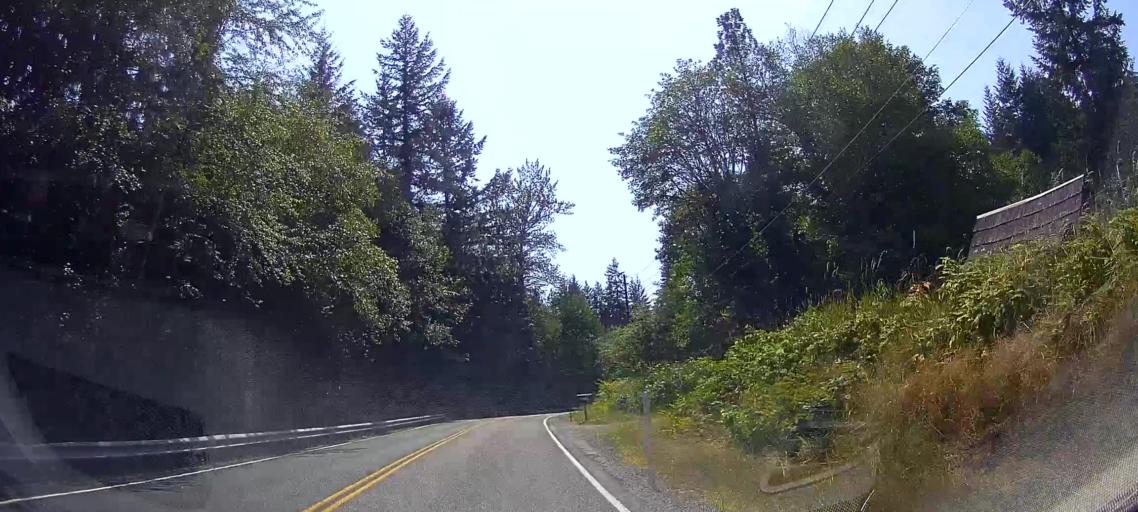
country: US
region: Washington
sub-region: Snohomish County
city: Bryant
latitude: 48.3305
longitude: -122.1373
